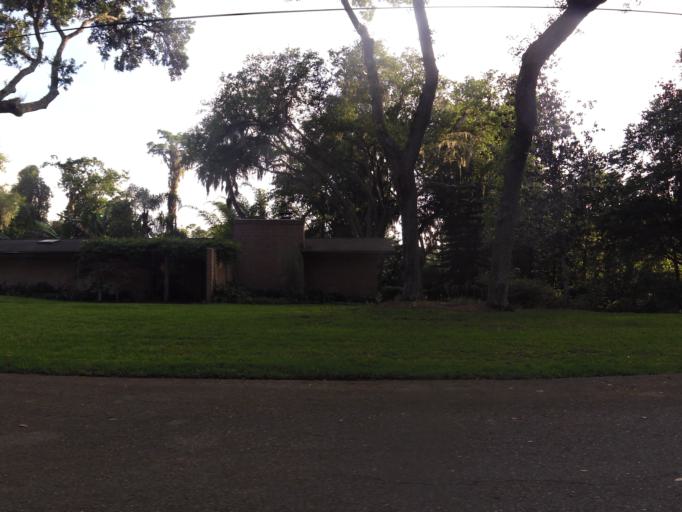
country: US
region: Florida
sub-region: Clay County
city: Orange Park
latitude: 30.2111
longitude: -81.6250
